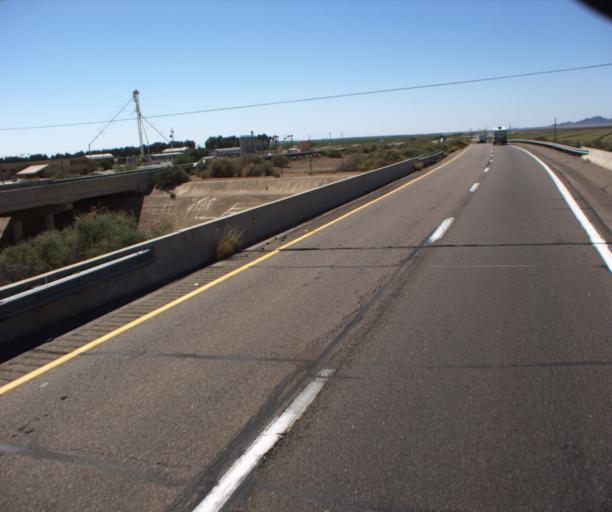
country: US
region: Arizona
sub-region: Maricopa County
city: Gila Bend
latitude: 32.9220
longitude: -112.8876
